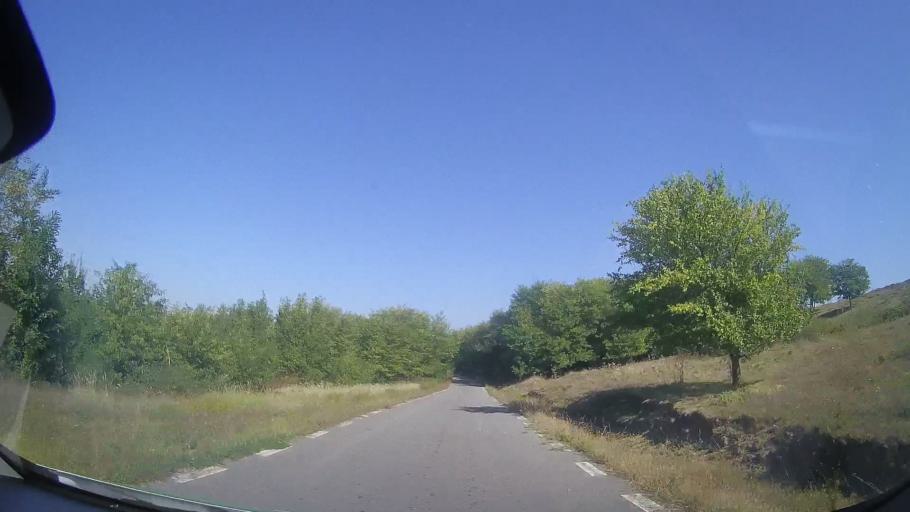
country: RO
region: Timis
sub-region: Comuna Ohaba Lunga
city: Ohaba Lunga
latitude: 45.9117
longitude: 21.9487
